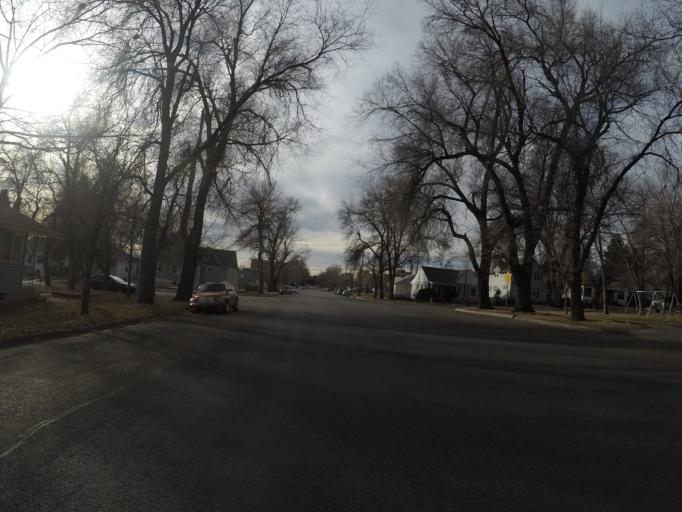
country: US
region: Montana
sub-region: Yellowstone County
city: Billings
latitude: 45.7949
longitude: -108.5142
